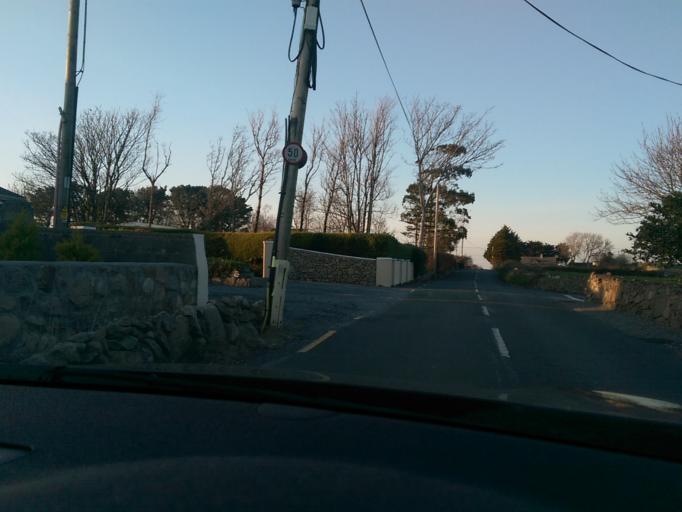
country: IE
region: Connaught
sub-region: County Galway
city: Gaillimh
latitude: 53.2812
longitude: -9.0829
